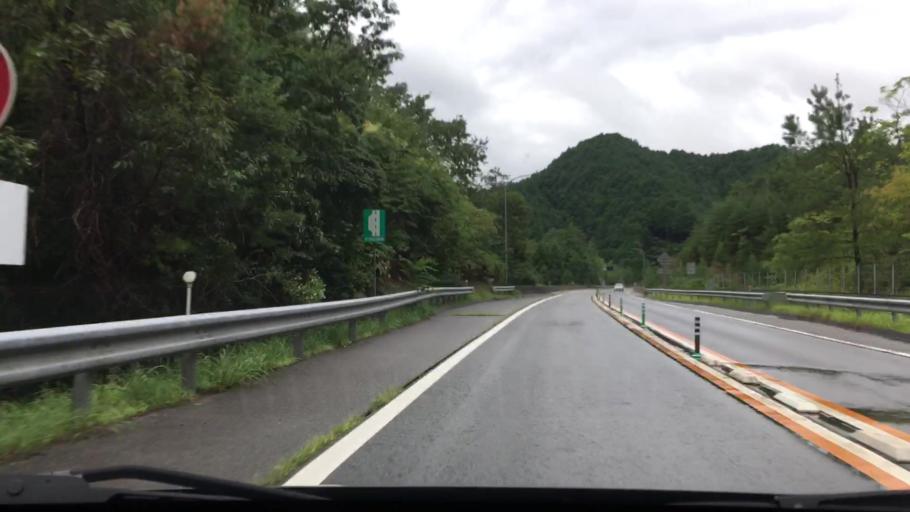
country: JP
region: Hyogo
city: Toyooka
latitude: 35.2665
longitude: 134.8057
